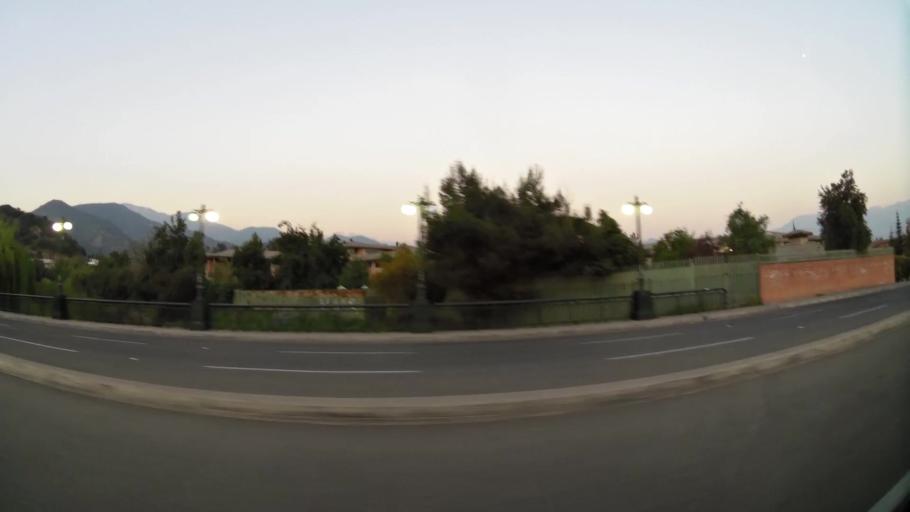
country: CL
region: Santiago Metropolitan
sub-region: Provincia de Chacabuco
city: Chicureo Abajo
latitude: -33.3244
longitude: -70.5424
